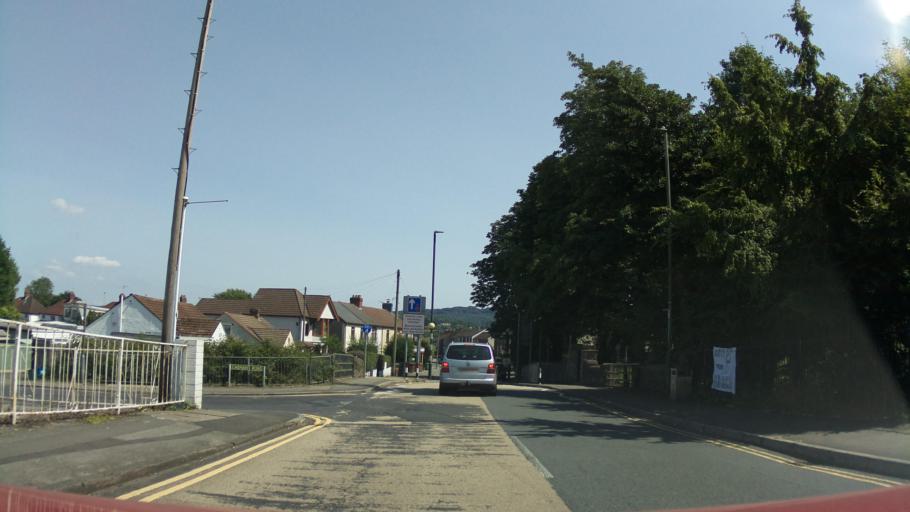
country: GB
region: Wales
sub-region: Caerphilly County Borough
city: Caerphilly
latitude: 51.5804
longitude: -3.2259
